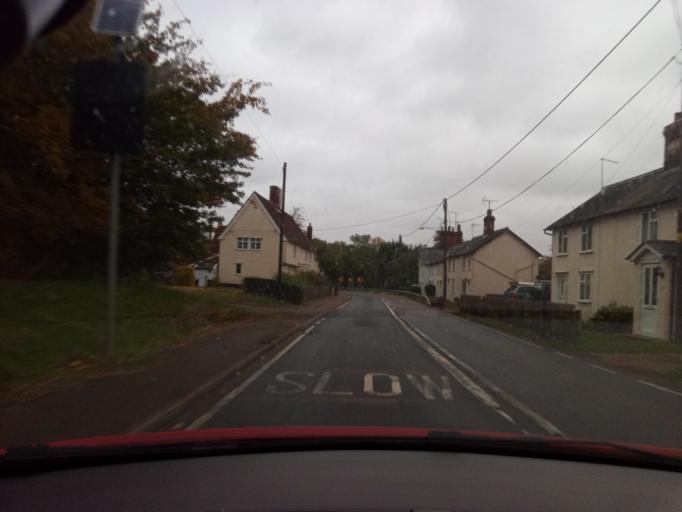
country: GB
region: England
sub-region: Suffolk
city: Kedington
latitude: 52.0564
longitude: 0.5136
